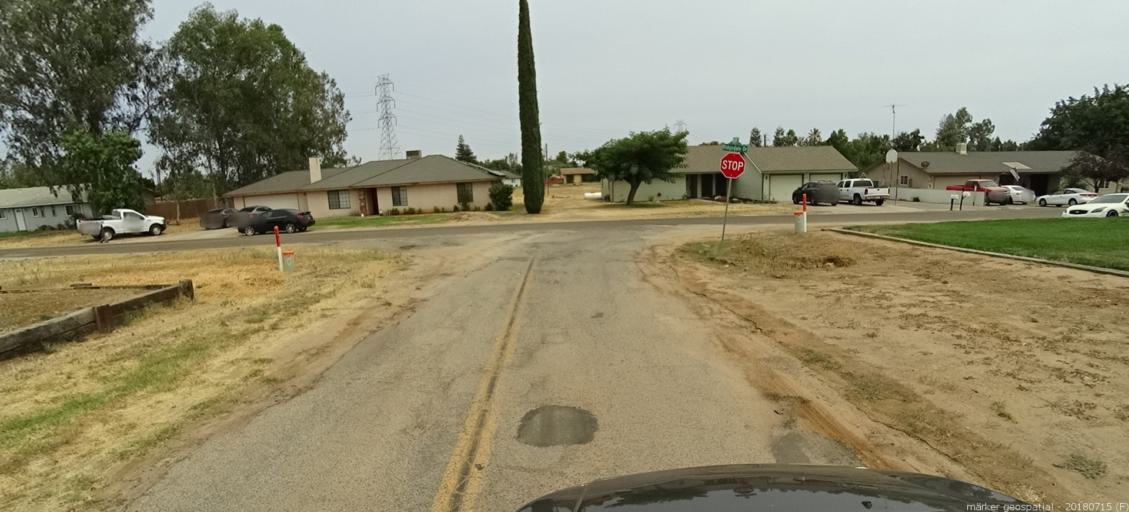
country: US
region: California
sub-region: Madera County
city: Madera Acres
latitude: 37.0135
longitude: -120.0802
